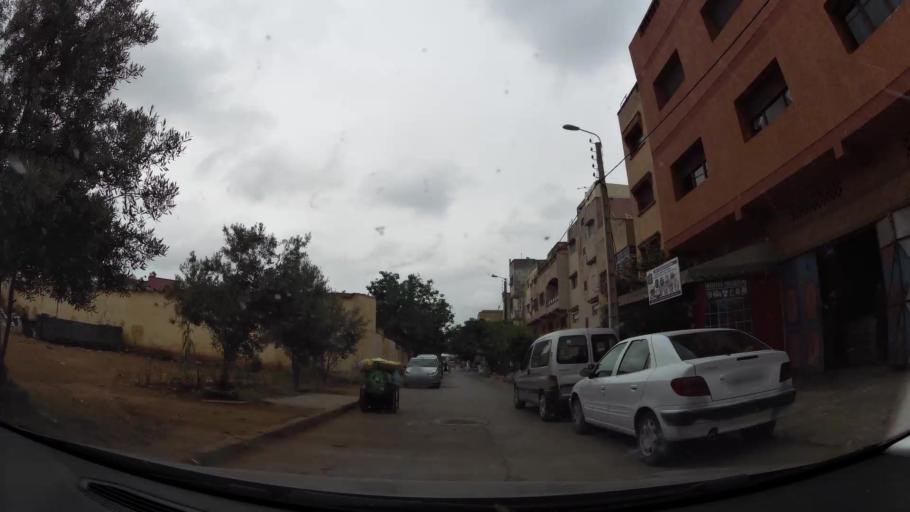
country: MA
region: Rabat-Sale-Zemmour-Zaer
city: Sale
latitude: 34.0452
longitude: -6.7954
